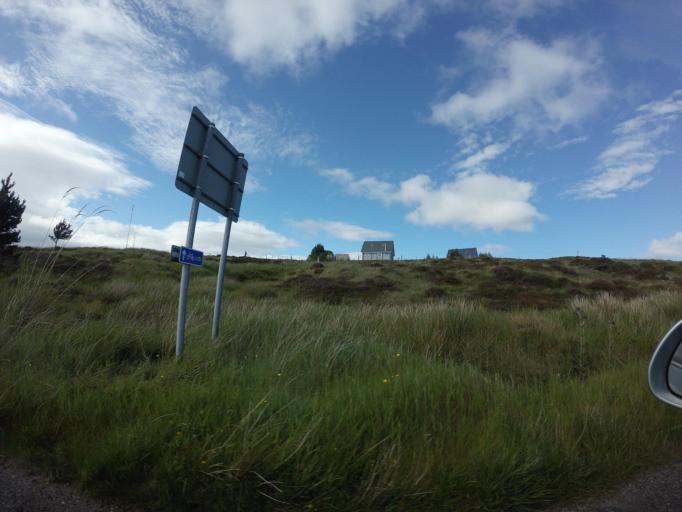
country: GB
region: Scotland
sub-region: Eilean Siar
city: Stornoway
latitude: 58.1716
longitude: -6.5743
